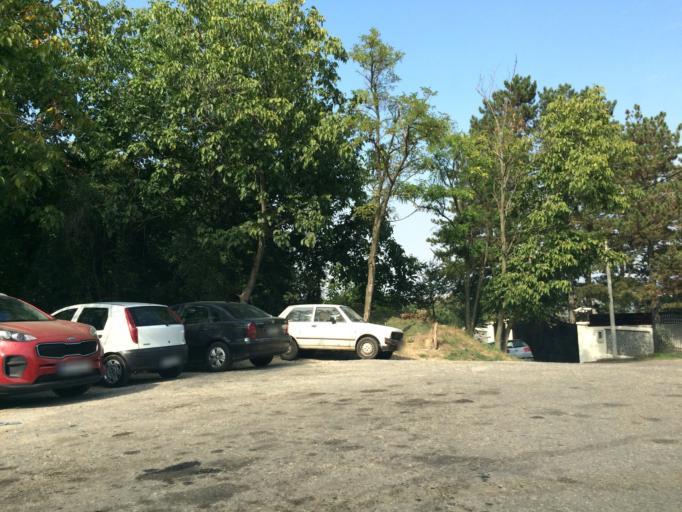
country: RS
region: Autonomna Pokrajina Vojvodina
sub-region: Juznobacki Okrug
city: Novi Sad
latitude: 45.1849
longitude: 19.8228
